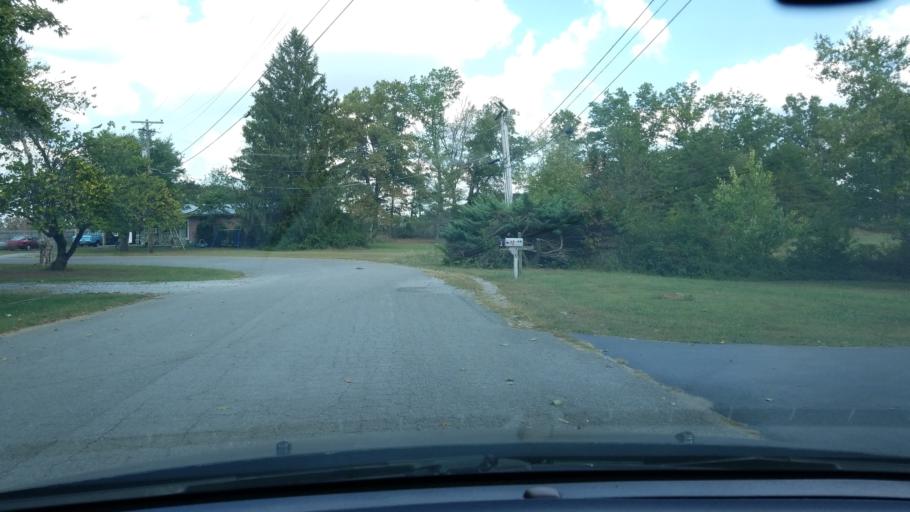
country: US
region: Tennessee
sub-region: Cumberland County
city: Crossville
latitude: 35.9640
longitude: -85.0674
